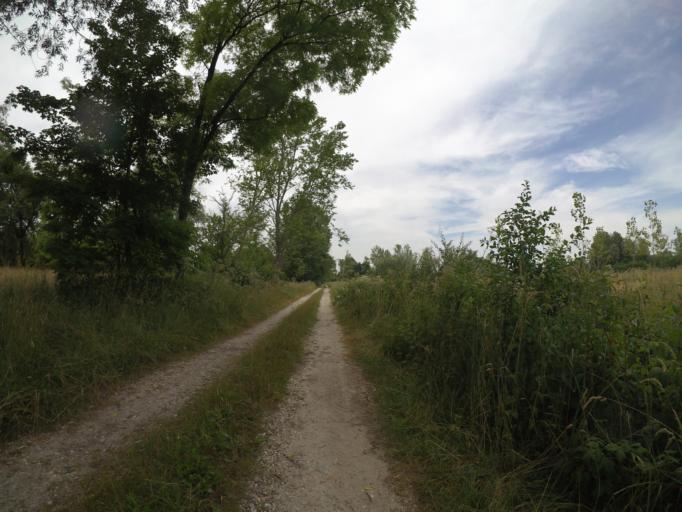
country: IT
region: Friuli Venezia Giulia
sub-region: Provincia di Udine
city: Bertiolo
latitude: 45.9252
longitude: 13.0588
